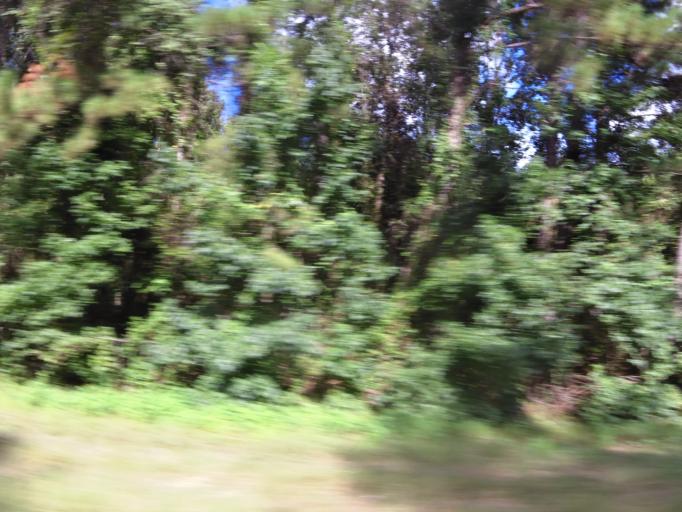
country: US
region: Georgia
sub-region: Camden County
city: Woodbine
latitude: 30.9212
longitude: -81.7141
